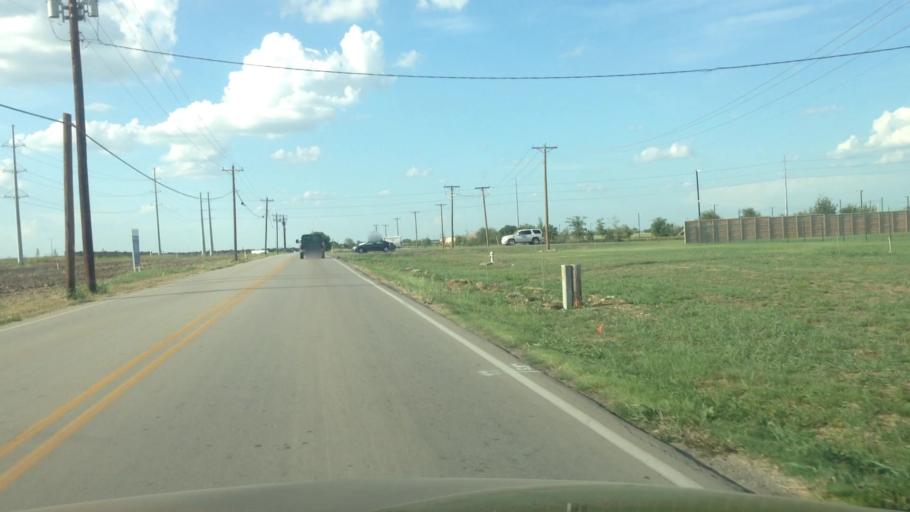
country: US
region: Texas
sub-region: Tarrant County
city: Haslet
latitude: 32.9420
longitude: -97.3920
